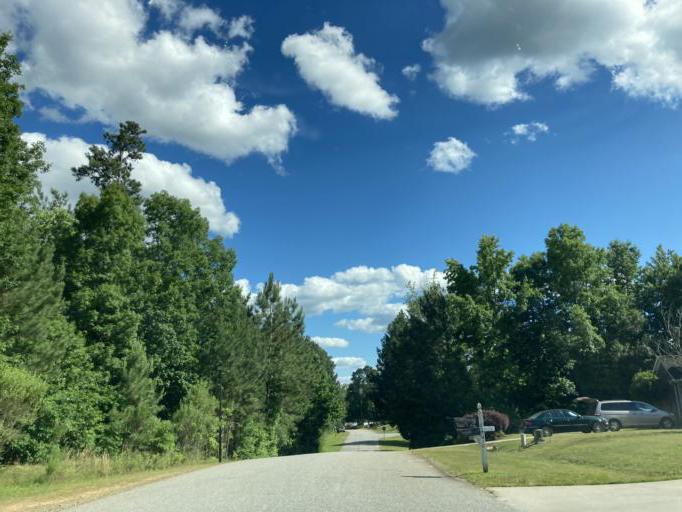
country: US
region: Georgia
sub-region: Jones County
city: Gray
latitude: 32.9981
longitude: -83.5486
